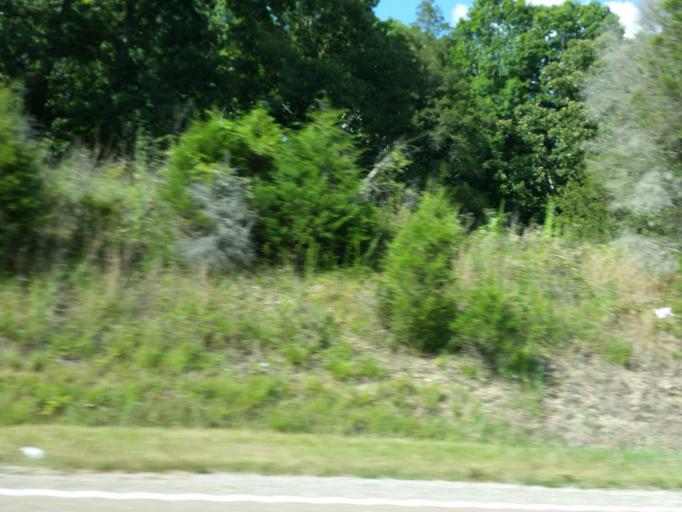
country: US
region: Tennessee
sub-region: Decatur County
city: Parsons
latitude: 35.6377
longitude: -88.0787
